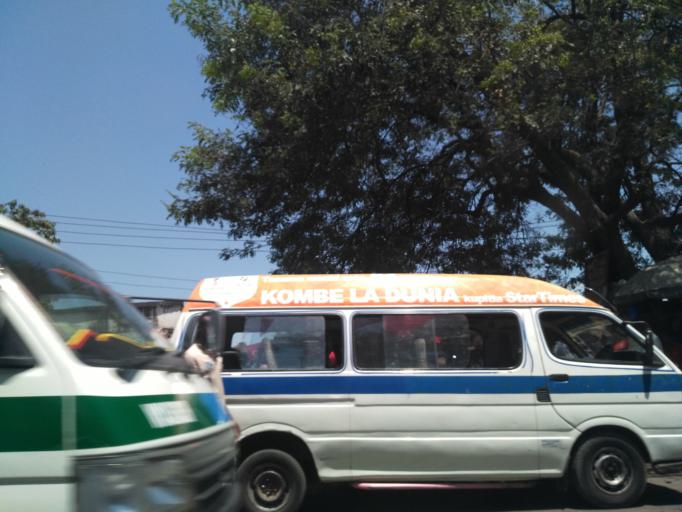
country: TZ
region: Mwanza
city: Mwanza
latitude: -2.5218
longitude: 32.9044
